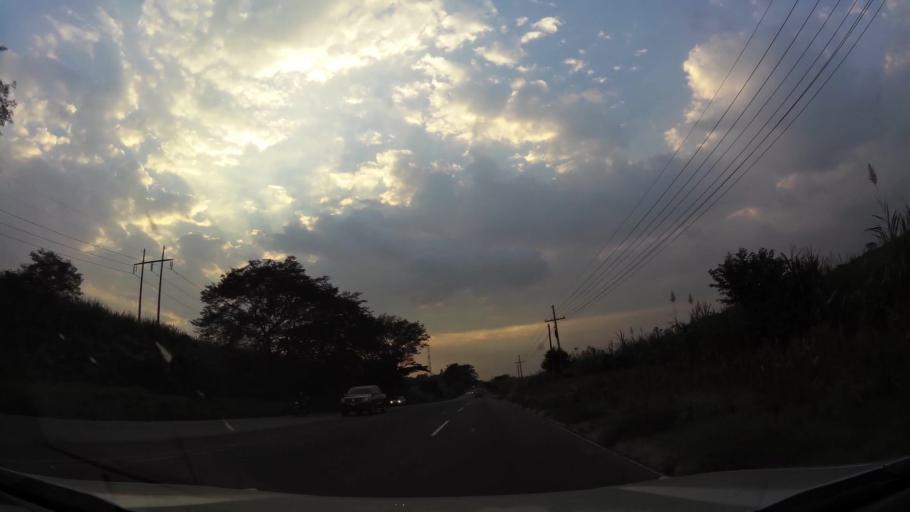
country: GT
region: Escuintla
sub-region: Municipio de Masagua
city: Masagua
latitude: 14.2674
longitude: -90.8802
